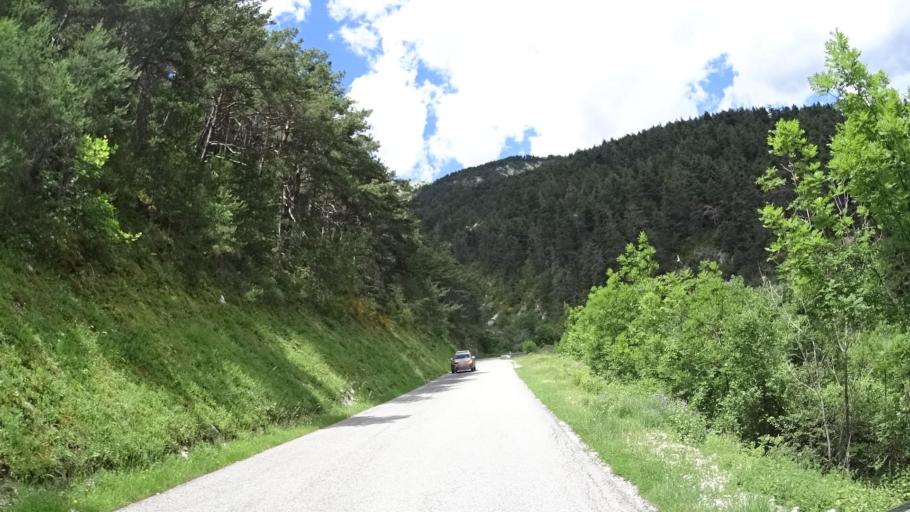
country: FR
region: Provence-Alpes-Cote d'Azur
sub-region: Departement des Alpes-de-Haute-Provence
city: Annot
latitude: 44.0205
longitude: 6.6201
